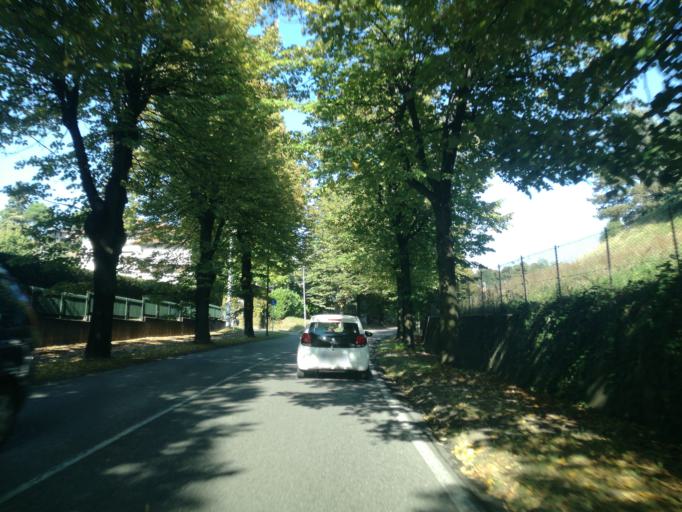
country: IT
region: Lombardy
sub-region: Provincia di Lecco
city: Robbiate
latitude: 45.6956
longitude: 9.4388
